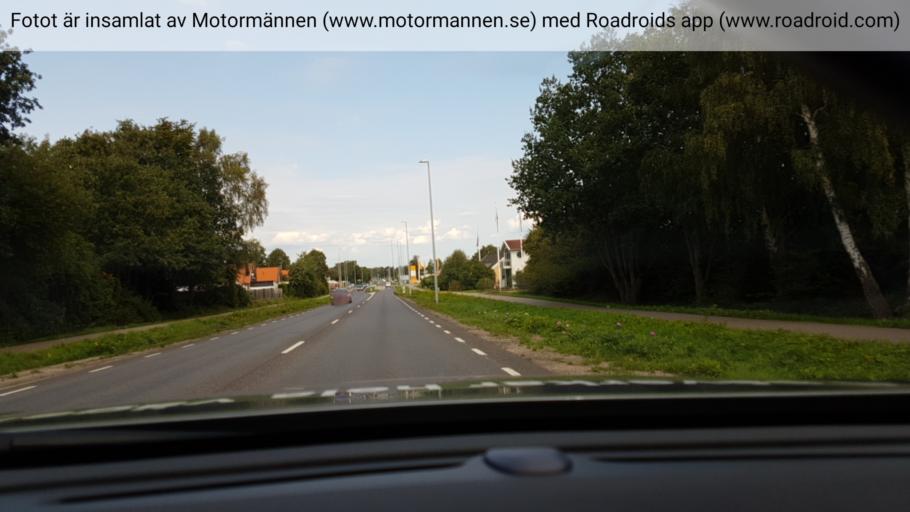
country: SE
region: Halland
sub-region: Halmstads Kommun
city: Mjallby
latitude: 56.6581
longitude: 12.8031
